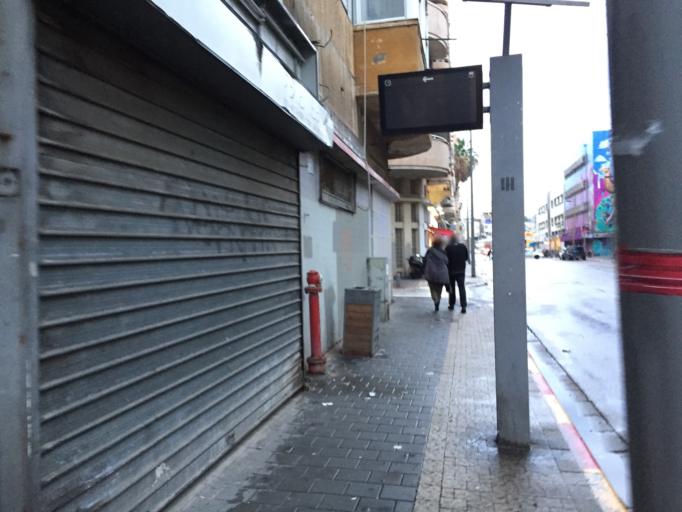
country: IL
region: Tel Aviv
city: Yafo
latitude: 32.0548
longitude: 34.7687
